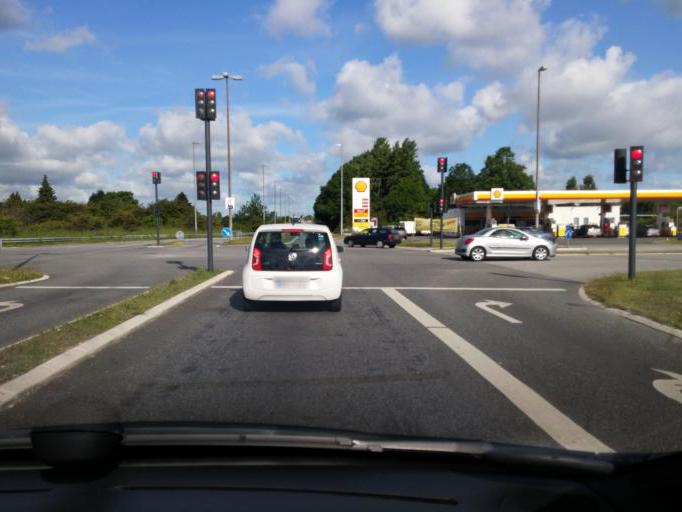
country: DK
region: Zealand
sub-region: Greve Kommune
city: Greve
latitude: 55.6003
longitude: 12.3091
